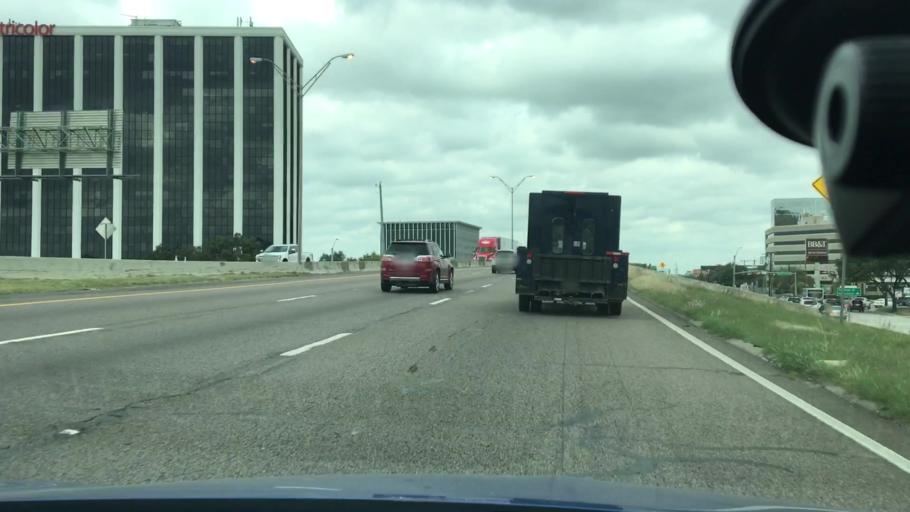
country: US
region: Texas
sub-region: Dallas County
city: Dallas
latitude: 32.8177
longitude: -96.8686
